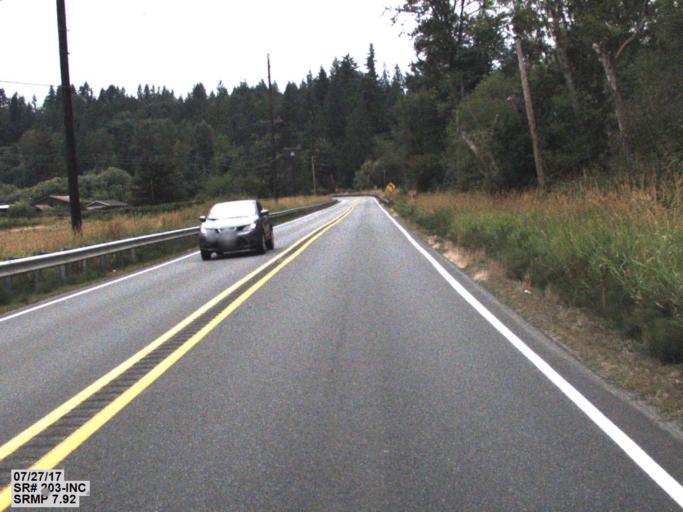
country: US
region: Washington
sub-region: King County
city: Lake Marcel-Stillwater
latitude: 47.6752
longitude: -121.9069
